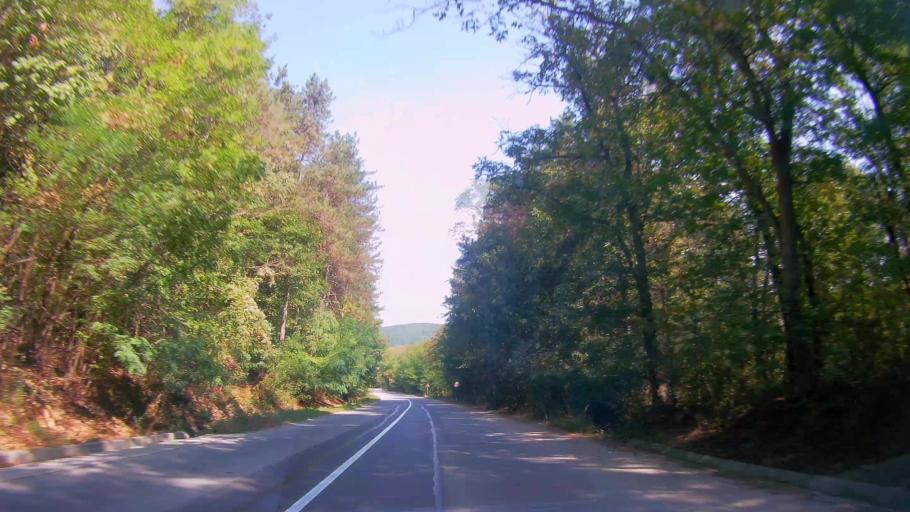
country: BG
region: Shumen
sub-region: Obshtina Smyadovo
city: Smyadovo
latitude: 43.0169
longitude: 27.0490
